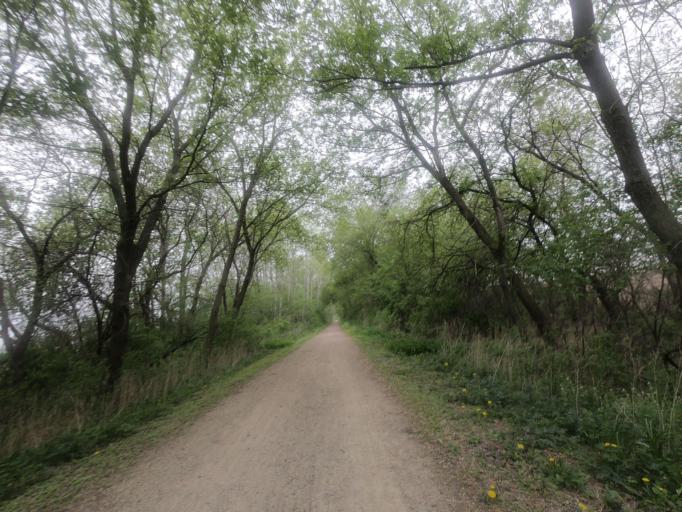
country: US
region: Wisconsin
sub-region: Jefferson County
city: Jefferson
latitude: 43.0366
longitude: -88.8158
